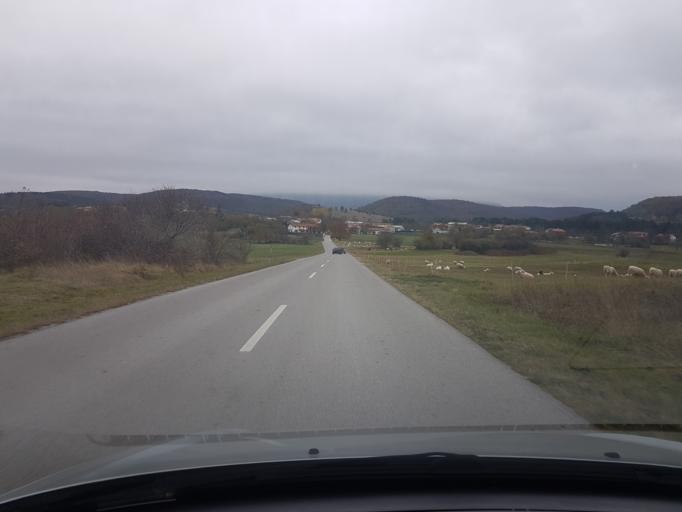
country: SI
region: Divaca
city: Divaca
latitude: 45.7271
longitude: 14.0073
